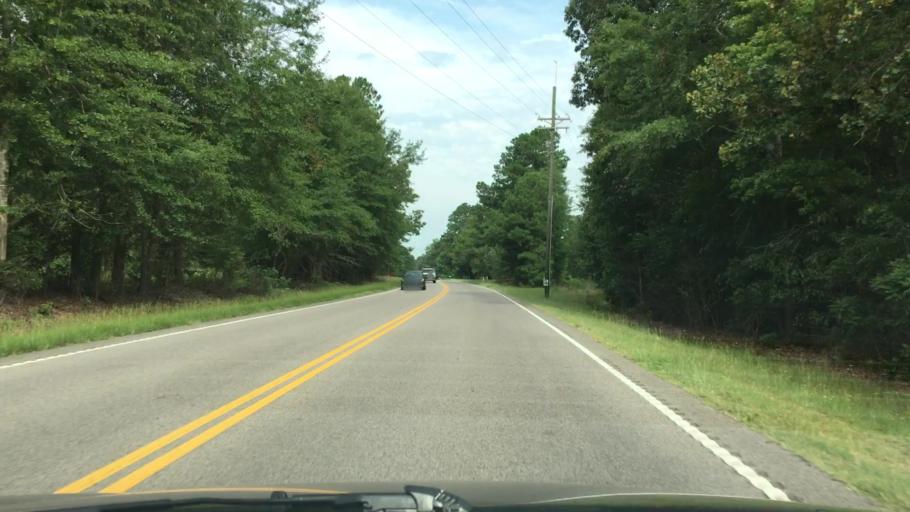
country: US
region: South Carolina
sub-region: Barnwell County
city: Williston
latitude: 33.6700
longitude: -81.4057
